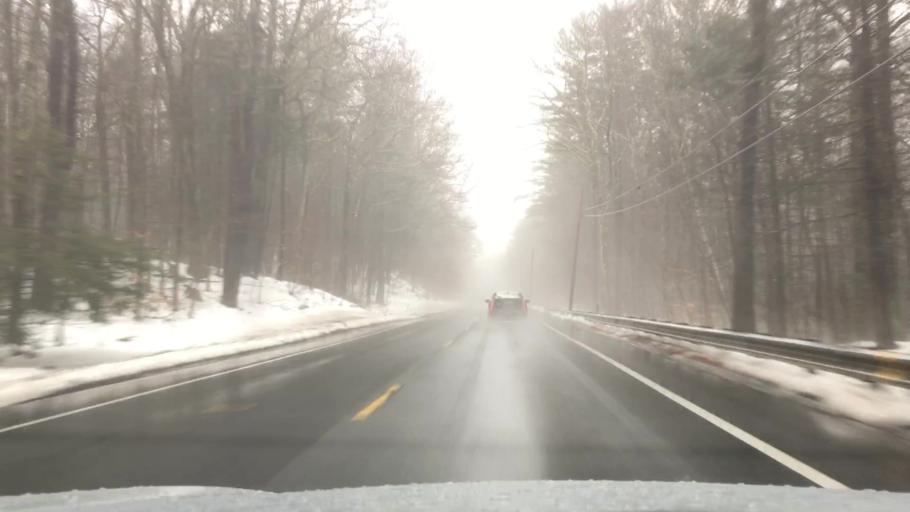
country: US
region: Massachusetts
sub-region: Franklin County
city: Orange
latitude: 42.5252
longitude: -72.3222
